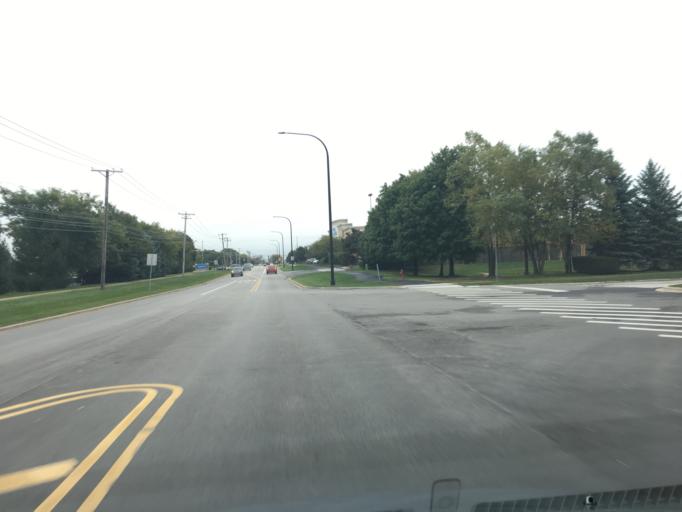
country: US
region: Illinois
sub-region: Will County
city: Plainfield
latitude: 41.6515
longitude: -88.2083
